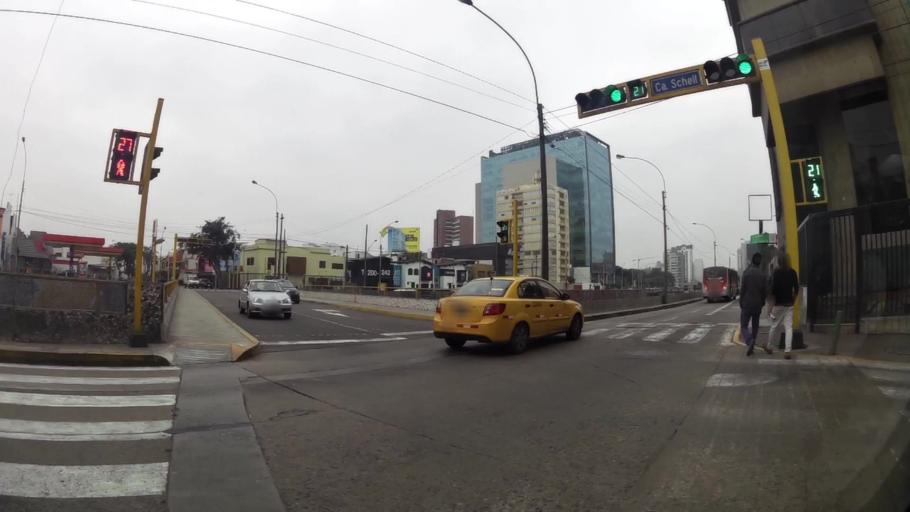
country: PE
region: Lima
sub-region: Lima
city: Surco
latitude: -12.1237
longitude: -77.0249
